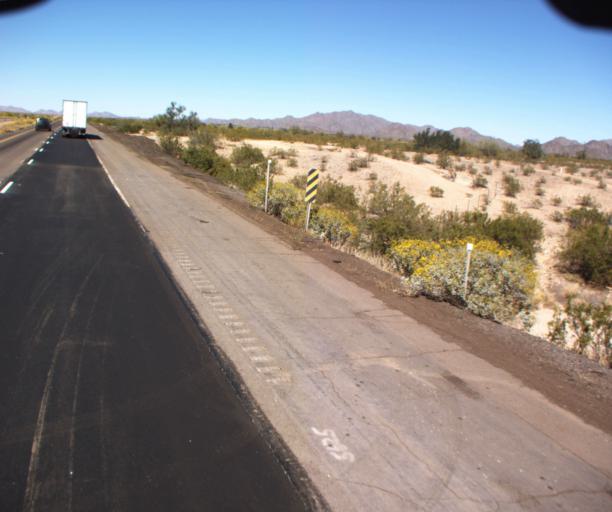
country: US
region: Arizona
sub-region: Maricopa County
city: Gila Bend
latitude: 33.0647
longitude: -112.6451
